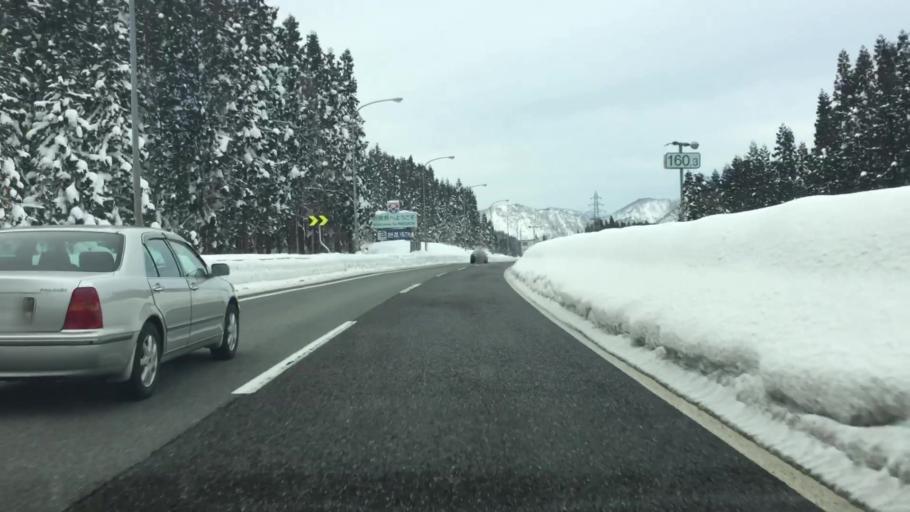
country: JP
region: Niigata
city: Shiozawa
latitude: 36.8822
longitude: 138.8531
